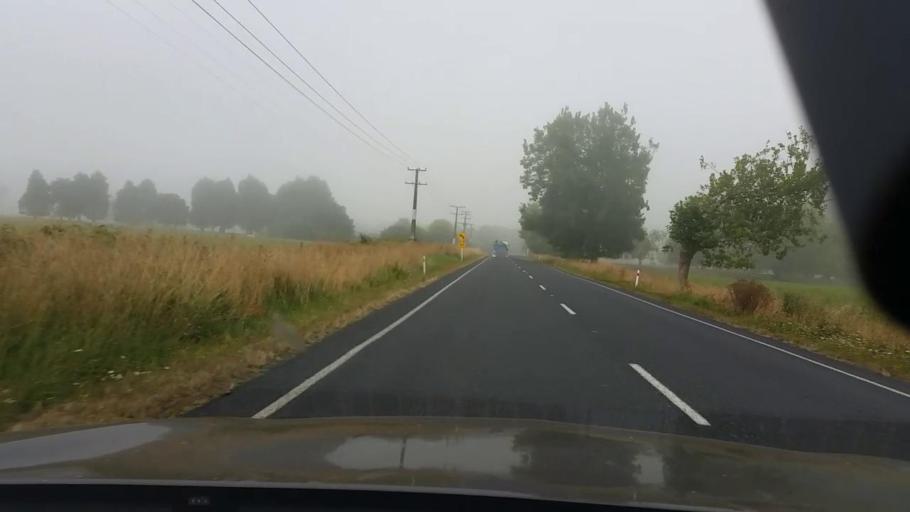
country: NZ
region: Waikato
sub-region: Waikato District
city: Ngaruawahia
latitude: -37.6365
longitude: 175.2999
